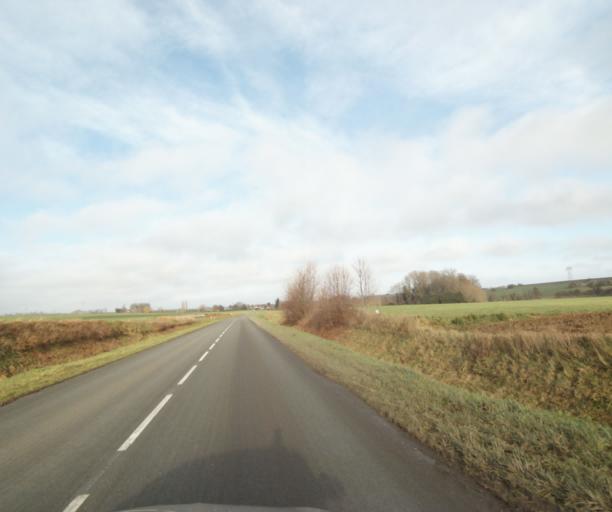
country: FR
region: Nord-Pas-de-Calais
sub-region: Departement du Nord
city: Thiant
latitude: 50.2747
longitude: 3.4543
